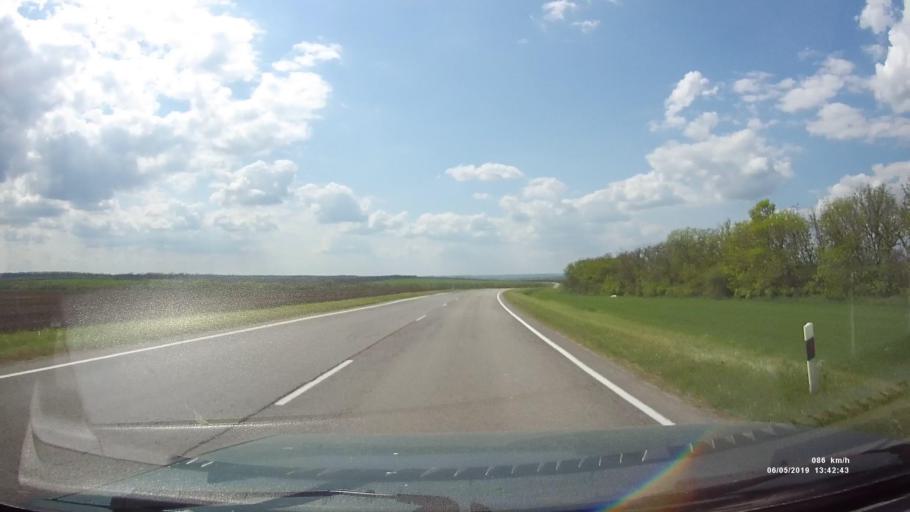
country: RU
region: Rostov
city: Semikarakorsk
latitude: 47.6589
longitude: 40.6527
